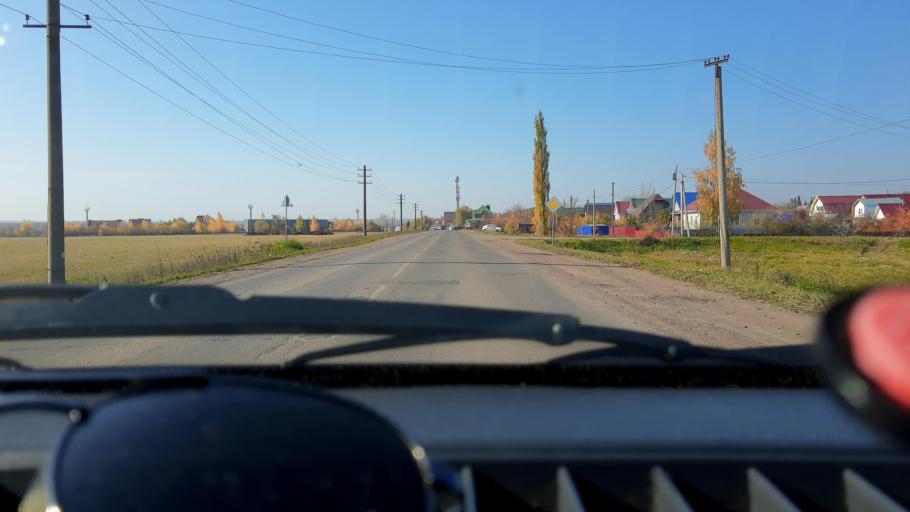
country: RU
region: Bashkortostan
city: Mikhaylovka
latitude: 54.8398
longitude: 55.8342
